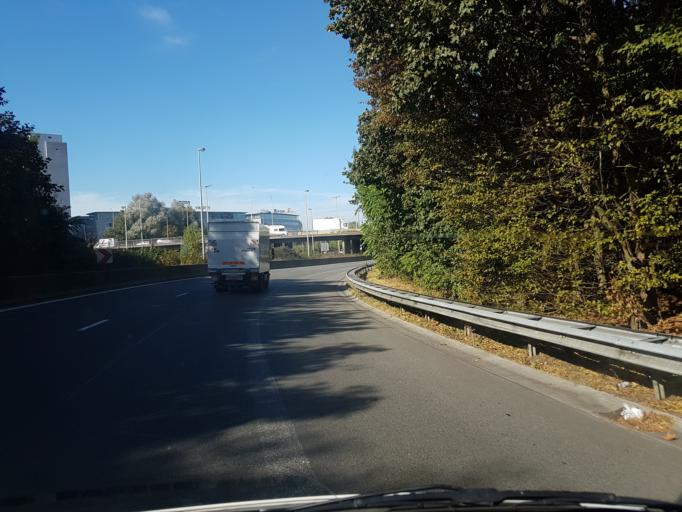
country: BE
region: Flanders
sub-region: Provincie Antwerpen
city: Borsbeek
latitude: 51.2173
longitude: 4.4520
